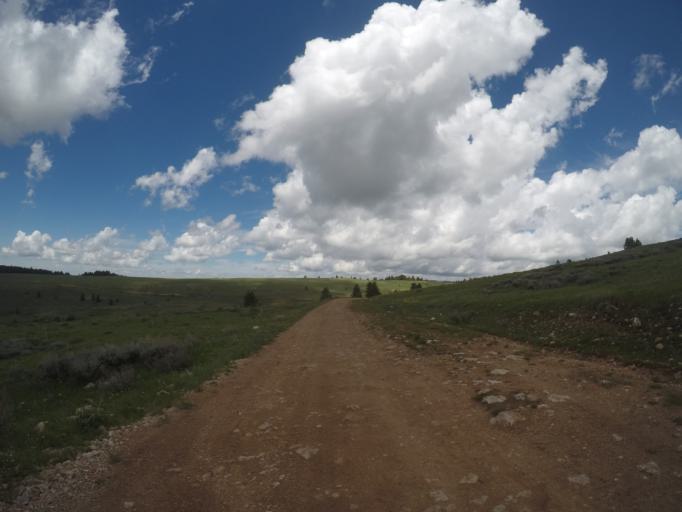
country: US
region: Wyoming
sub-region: Big Horn County
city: Lovell
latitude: 45.1767
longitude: -108.4377
